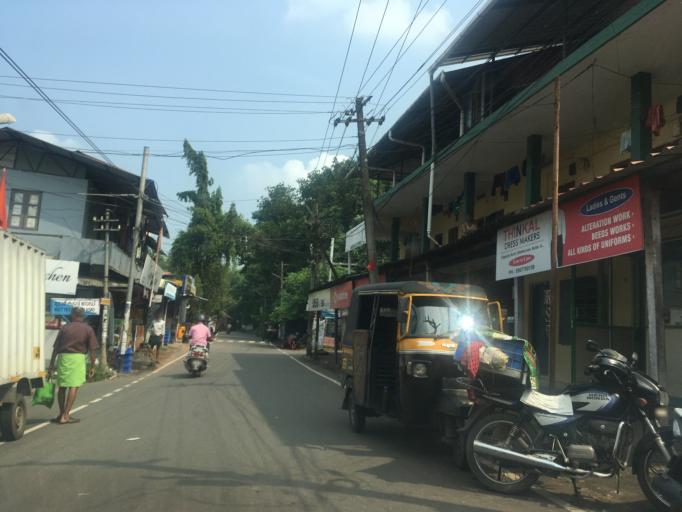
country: IN
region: Kerala
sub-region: Ernakulam
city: Elur
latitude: 10.0432
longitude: 76.3055
